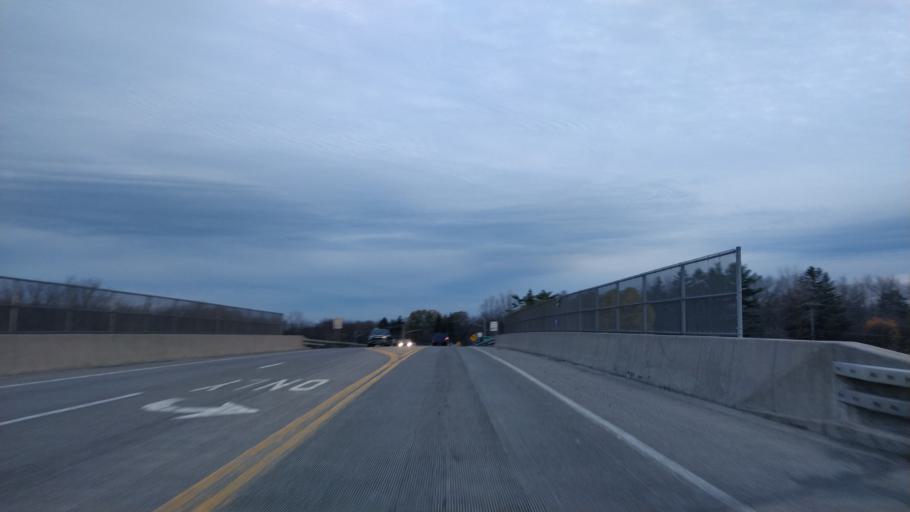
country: US
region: New York
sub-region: Onondaga County
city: Brewerton
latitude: 43.2321
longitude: -76.1296
